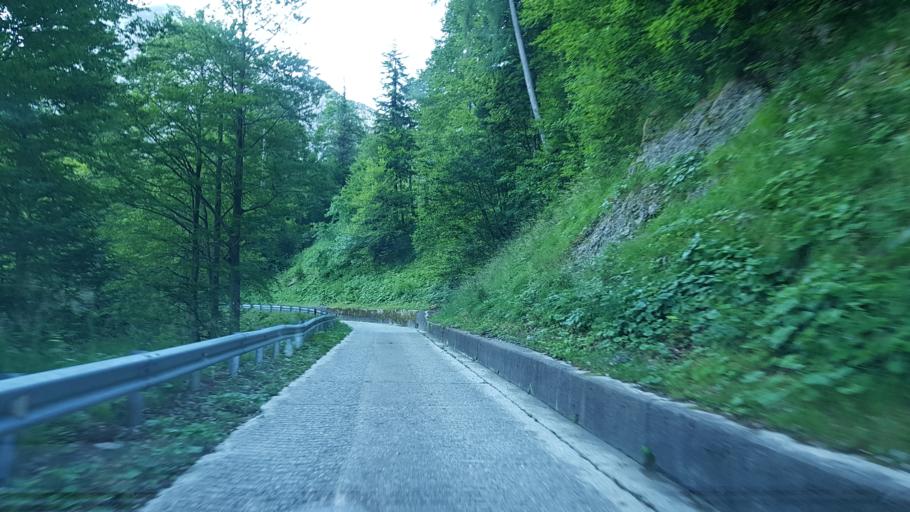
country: IT
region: Friuli Venezia Giulia
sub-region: Provincia di Udine
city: Pontebba
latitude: 46.4813
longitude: 13.2505
